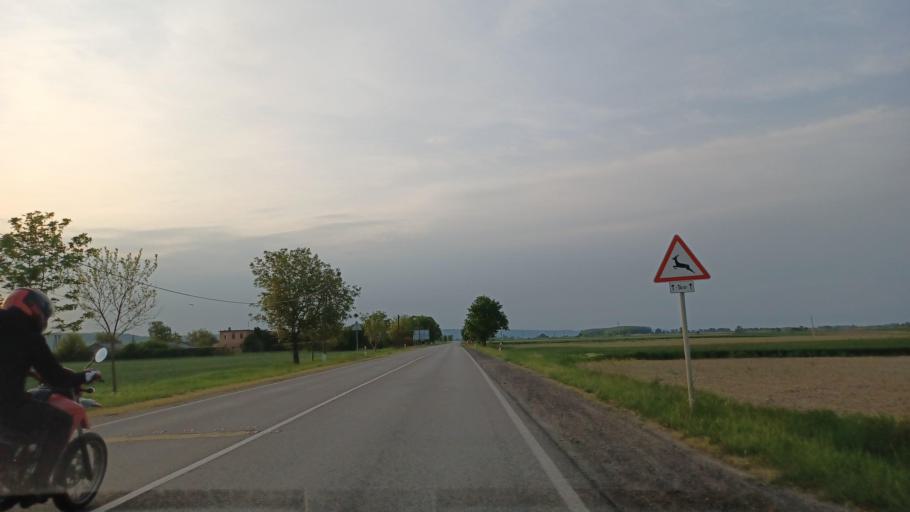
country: HU
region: Tolna
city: Bataszek
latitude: 46.2074
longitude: 18.7197
